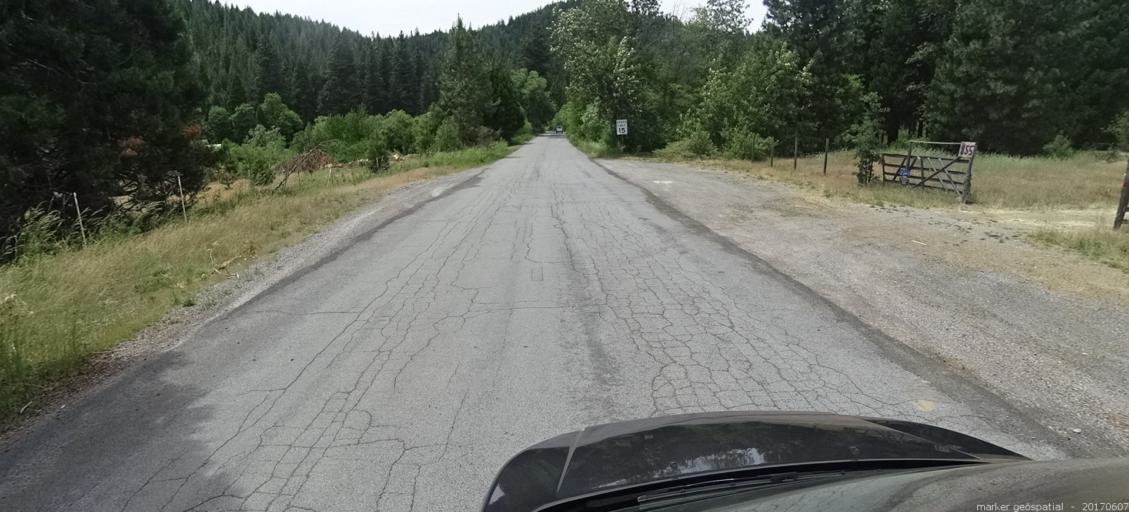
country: US
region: California
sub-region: Siskiyou County
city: Mount Shasta
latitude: 41.2941
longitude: -122.3235
